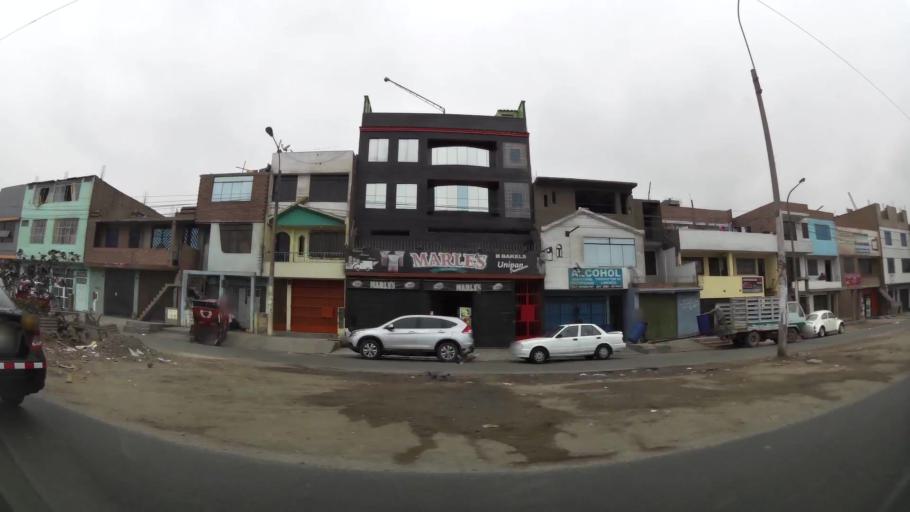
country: PE
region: Lima
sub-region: Lima
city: Independencia
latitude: -11.9541
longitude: -77.0602
